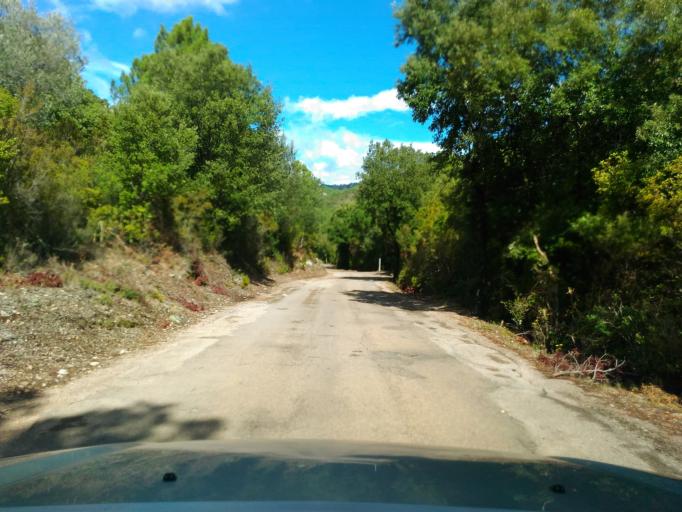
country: FR
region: Corsica
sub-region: Departement de la Corse-du-Sud
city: Porto-Vecchio
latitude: 41.7146
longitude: 9.3033
